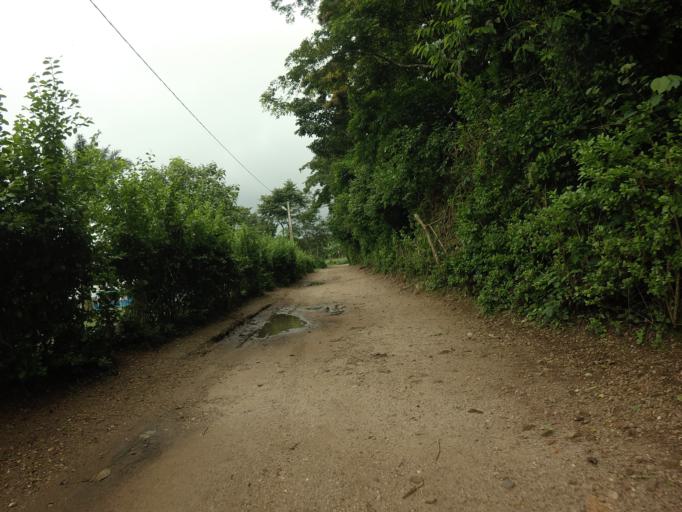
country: TG
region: Plateaux
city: Kpalime
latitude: 6.8467
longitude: 0.4419
